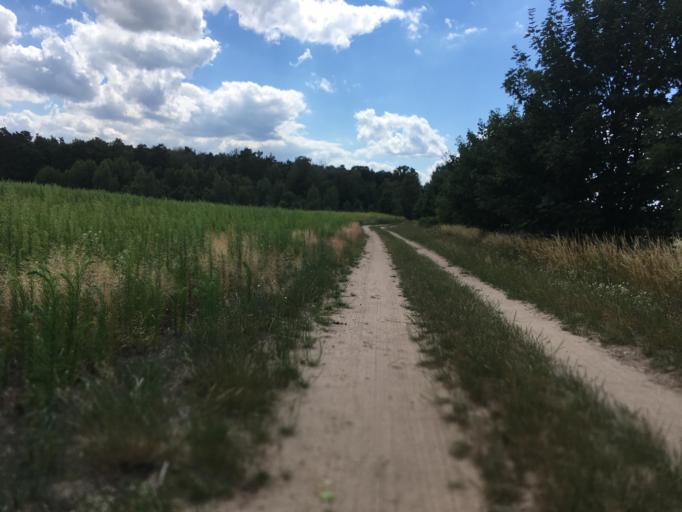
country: DE
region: Brandenburg
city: Joachimsthal
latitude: 52.9002
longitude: 13.7203
